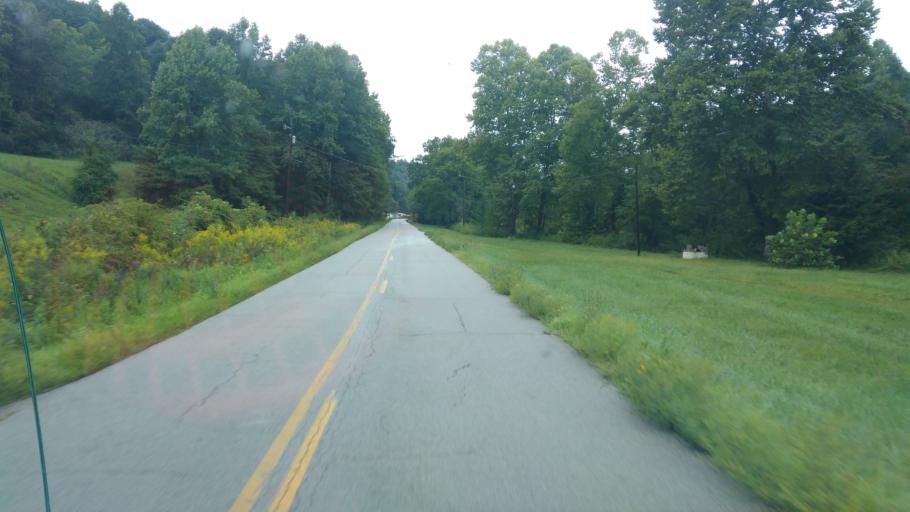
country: US
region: Kentucky
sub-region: Fleming County
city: Flemingsburg
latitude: 38.4255
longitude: -83.5142
